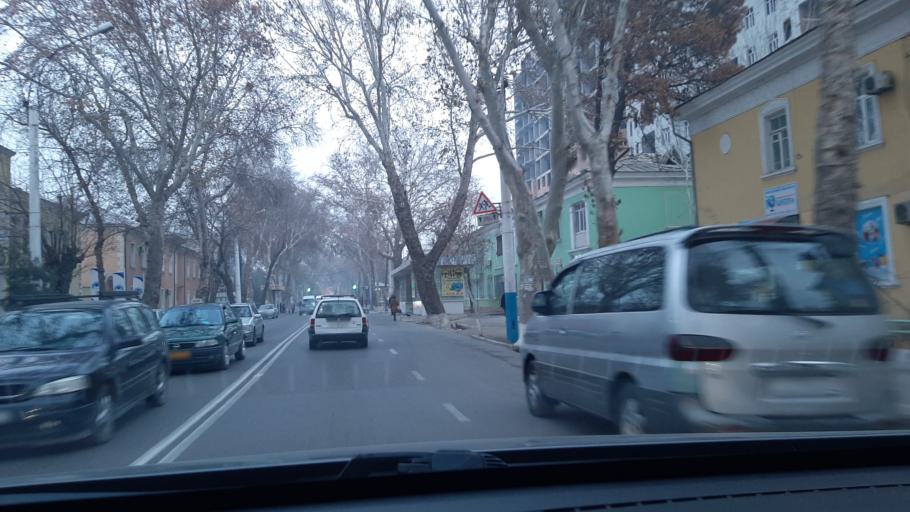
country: TJ
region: Viloyati Sughd
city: Khujand
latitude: 40.2808
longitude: 69.6197
